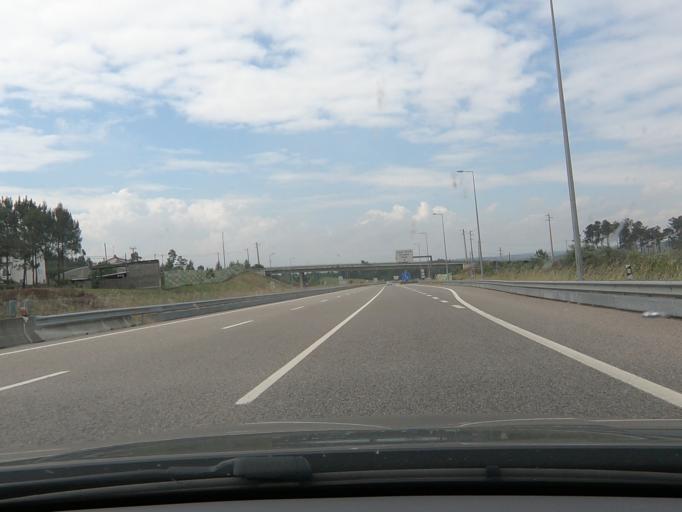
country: PT
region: Leiria
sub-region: Leiria
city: Amor
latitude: 39.8168
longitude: -8.8386
